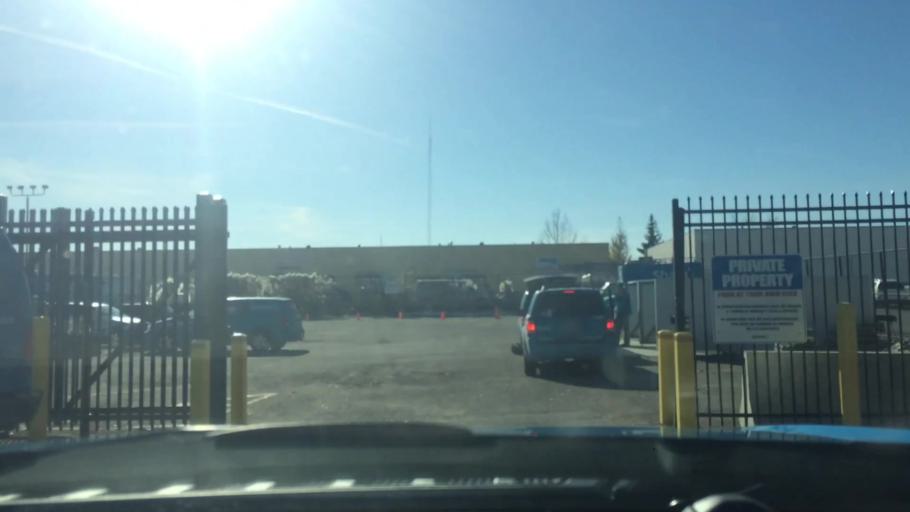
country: CA
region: Alberta
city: Calgary
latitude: 51.0764
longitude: -114.0117
